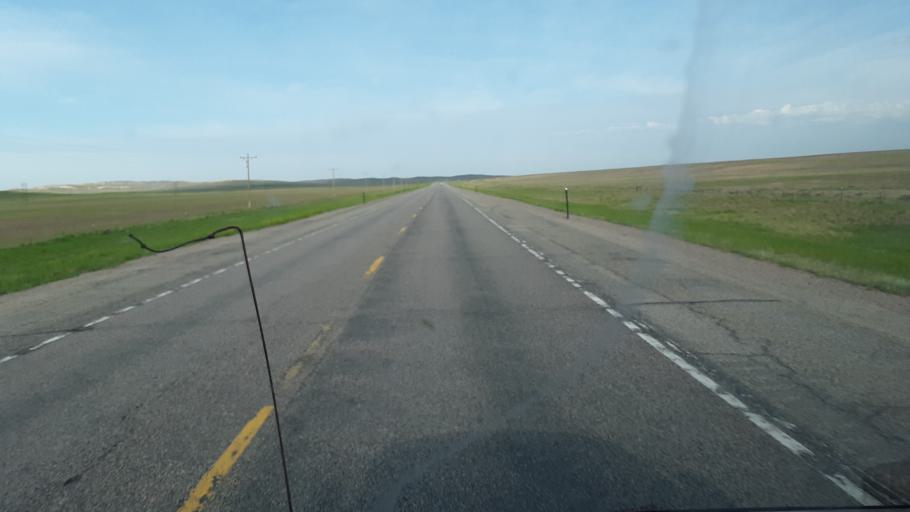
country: US
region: Wyoming
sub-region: Natrona County
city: Mills
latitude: 43.0273
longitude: -106.9345
